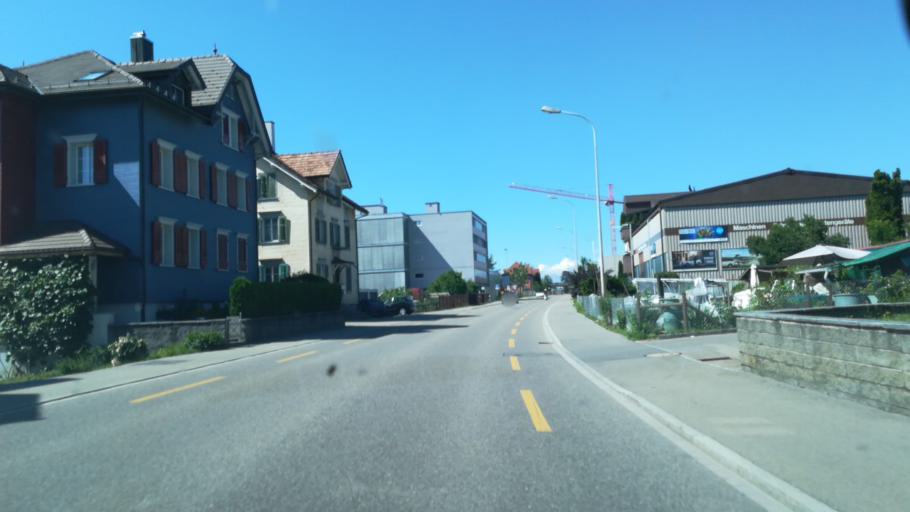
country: CH
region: Saint Gallen
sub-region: Wahlkreis St. Gallen
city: Gossau
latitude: 47.4207
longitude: 9.2416
